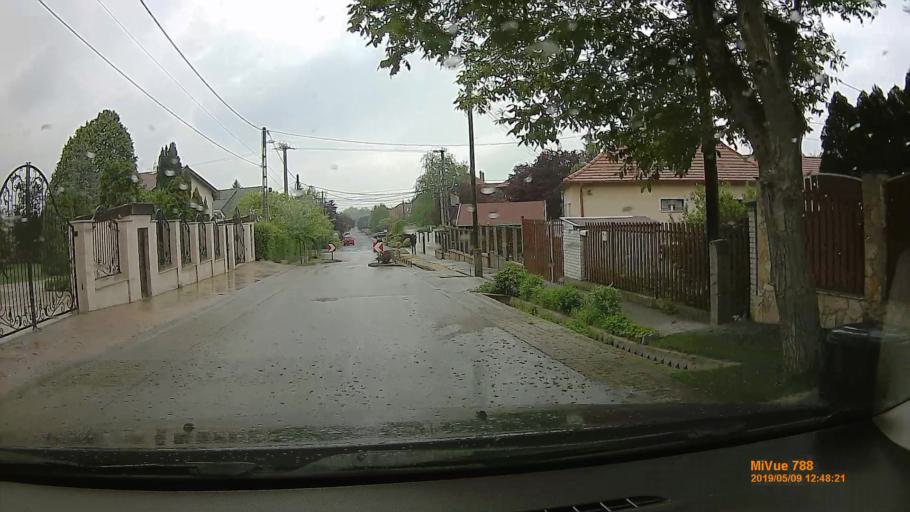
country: HU
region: Budapest
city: Budapest XVI. keruelet
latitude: 47.5379
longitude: 19.1813
